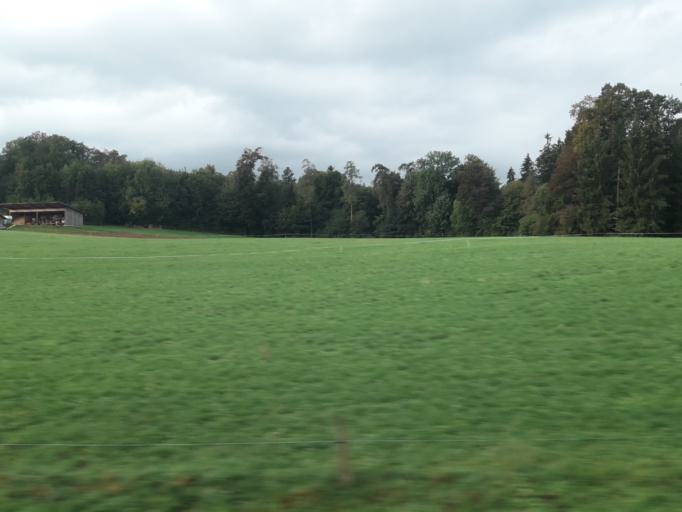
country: CH
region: Bern
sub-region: Thun District
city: Uetendorf
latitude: 46.7834
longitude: 7.5647
